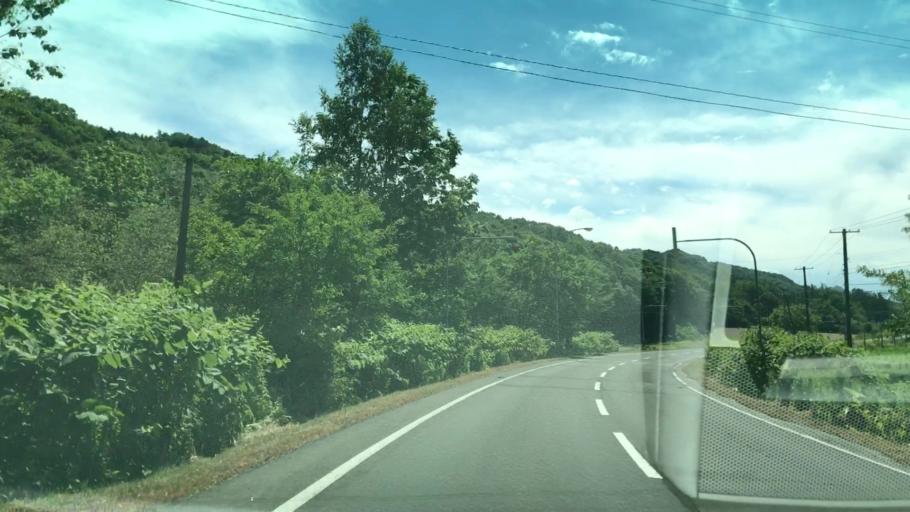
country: JP
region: Hokkaido
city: Shimo-furano
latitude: 42.9753
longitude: 142.4185
